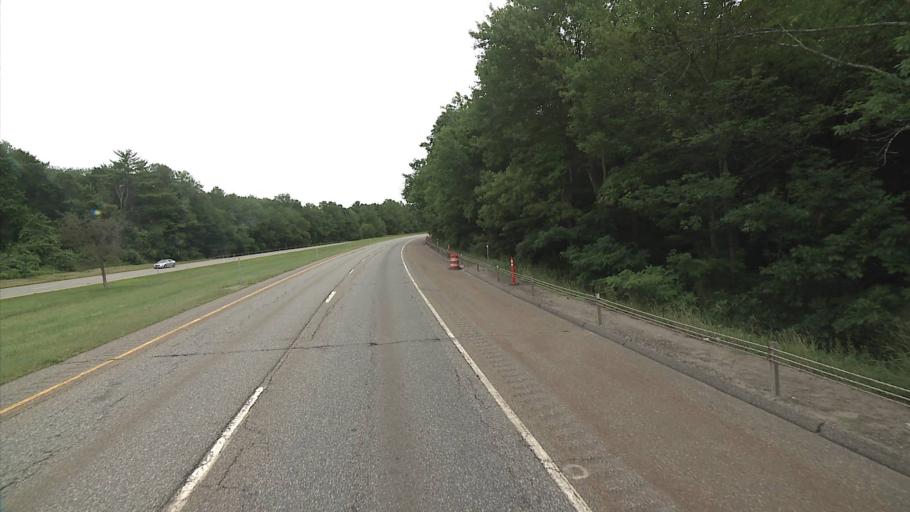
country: US
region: Connecticut
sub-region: Litchfield County
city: Thomaston
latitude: 41.7150
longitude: -73.0915
